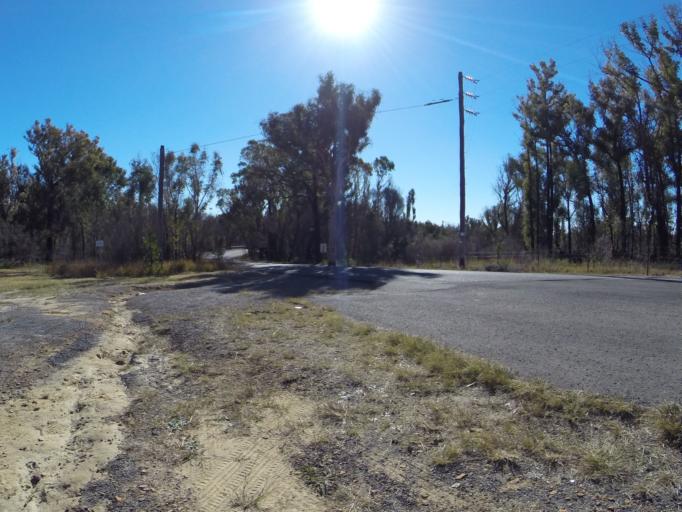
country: AU
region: New South Wales
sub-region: Wollondilly
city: Douglas Park
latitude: -34.3101
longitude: 150.7386
